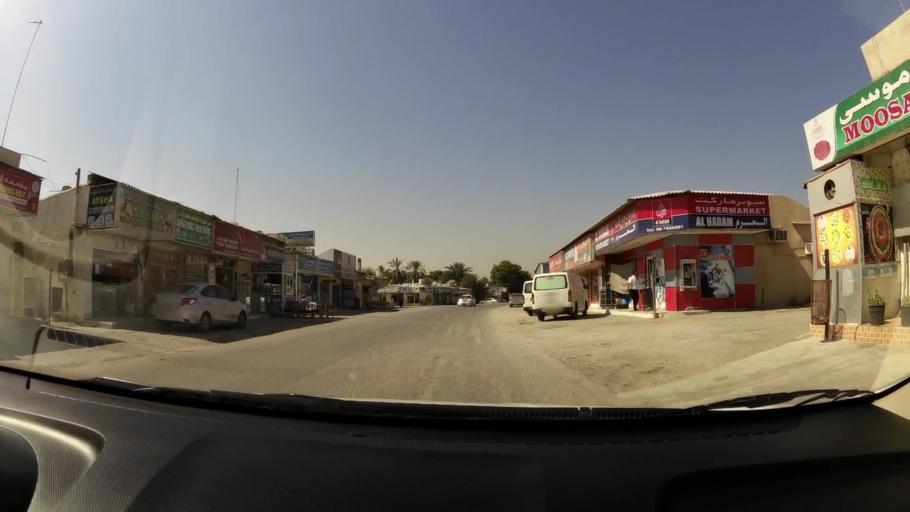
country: AE
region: Umm al Qaywayn
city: Umm al Qaywayn
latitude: 25.5851
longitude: 55.5760
